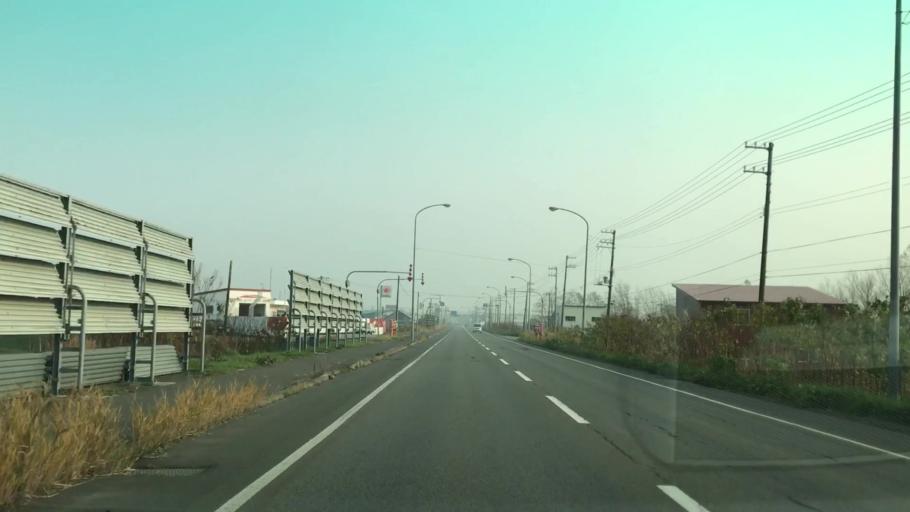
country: JP
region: Hokkaido
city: Ishikari
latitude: 43.2403
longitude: 141.3663
